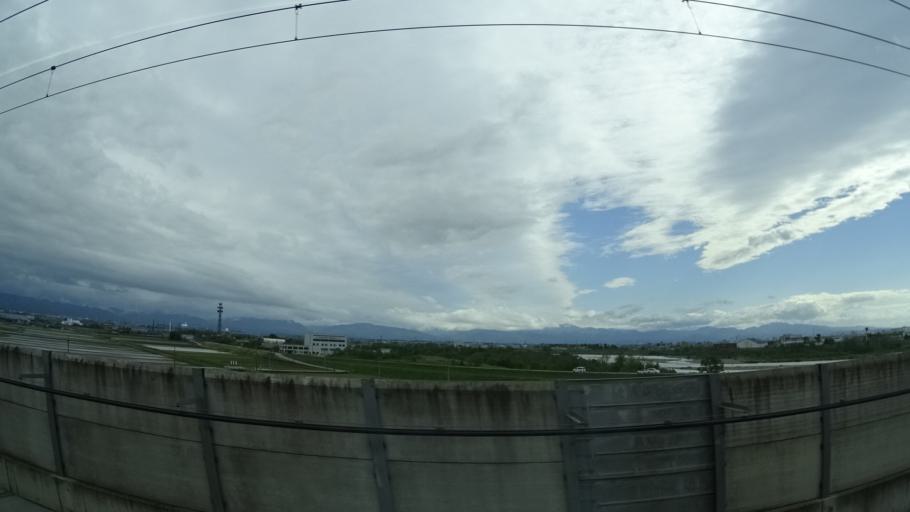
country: JP
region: Toyama
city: Toyama-shi
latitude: 36.7135
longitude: 137.2763
